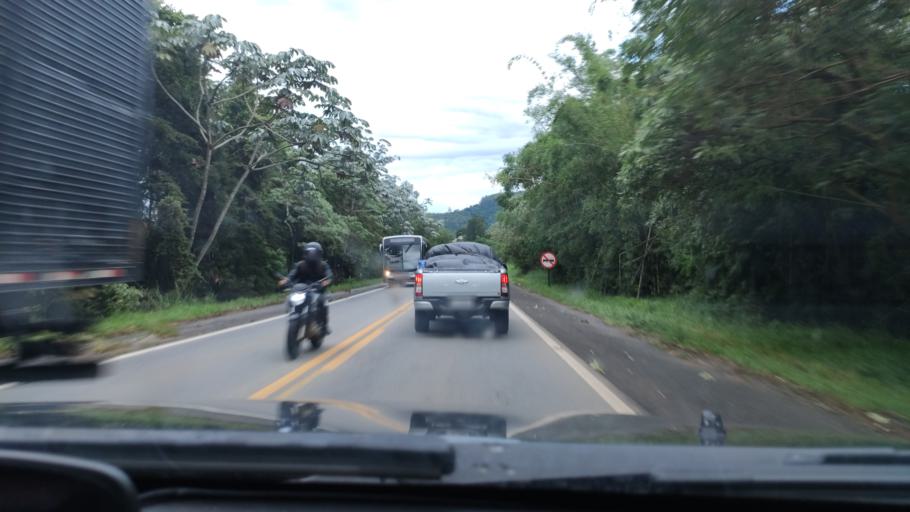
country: BR
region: Sao Paulo
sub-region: Braganca Paulista
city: Braganca Paulista
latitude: -22.8777
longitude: -46.5351
